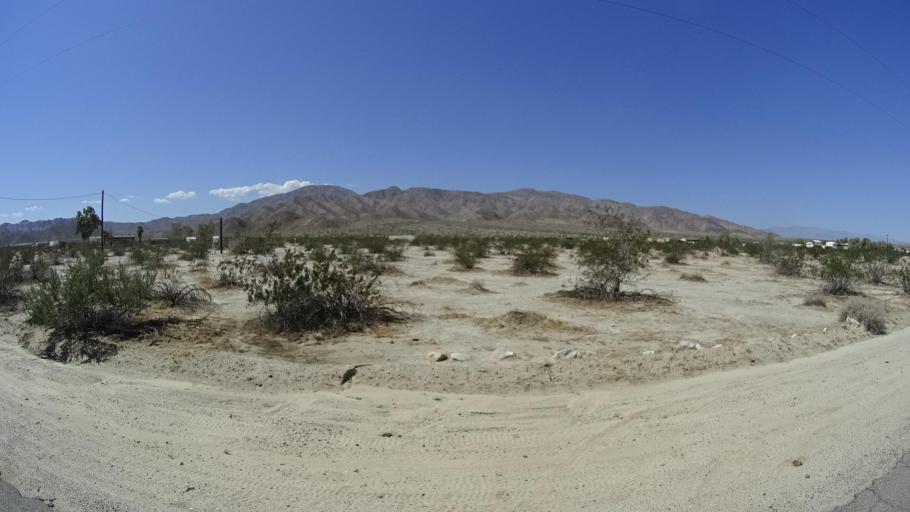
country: US
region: California
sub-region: Imperial County
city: Salton City
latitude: 33.0859
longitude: -116.1094
